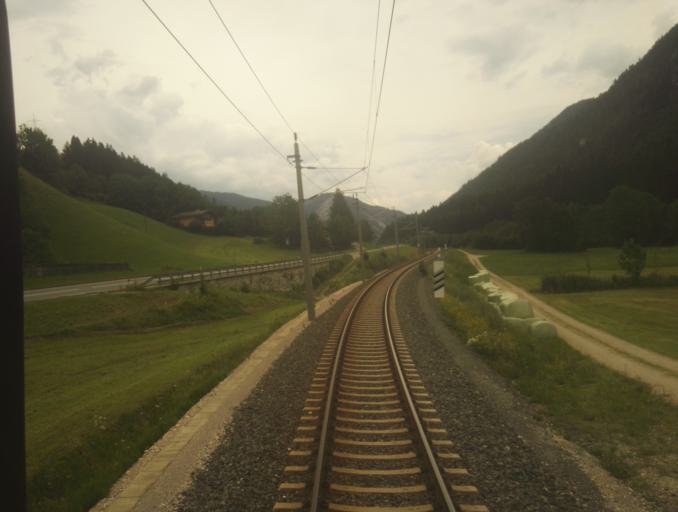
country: AT
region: Salzburg
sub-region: Politischer Bezirk Sankt Johann im Pongau
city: Forstau
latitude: 47.3996
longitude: 13.5412
